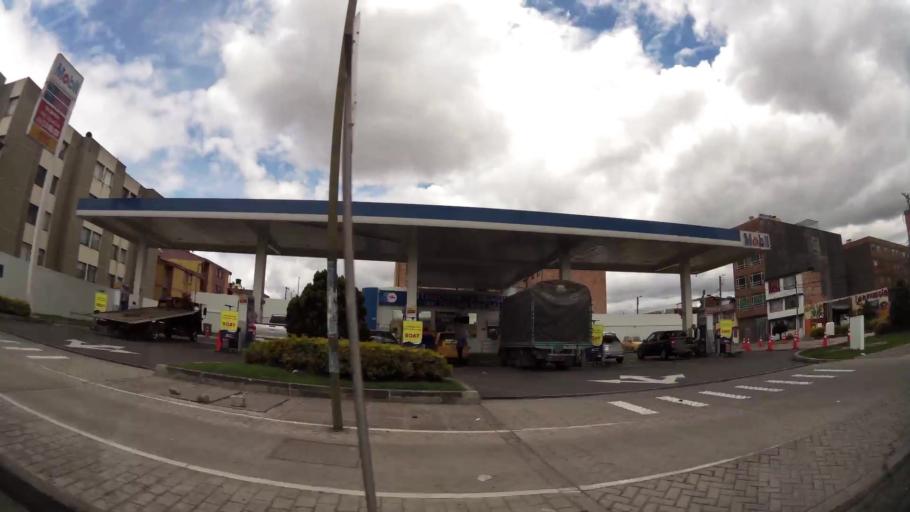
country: CO
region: Bogota D.C.
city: Barrio San Luis
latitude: 4.7084
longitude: -74.0960
